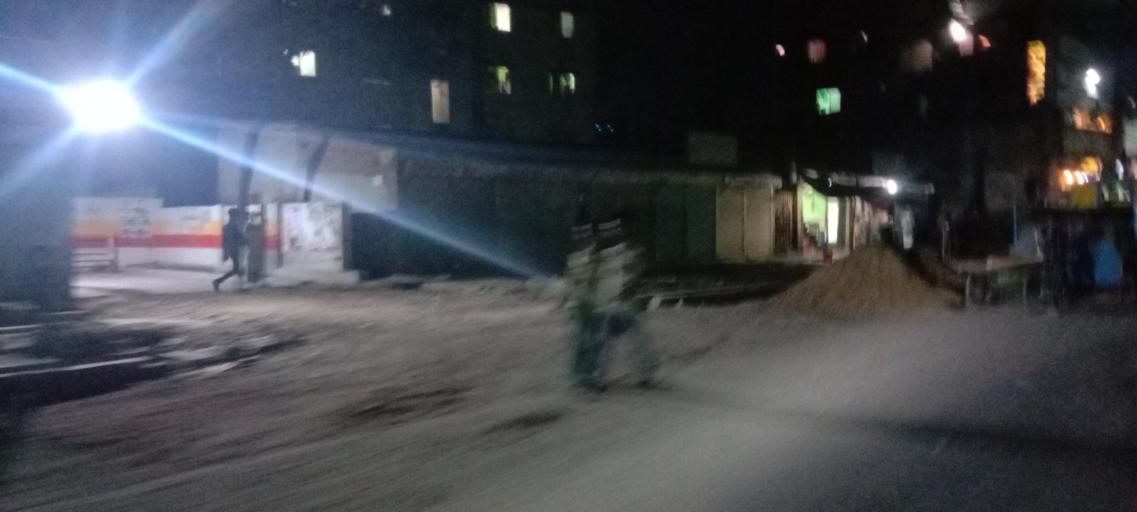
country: BD
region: Dhaka
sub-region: Dhaka
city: Dhaka
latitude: 23.7010
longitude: 90.3945
